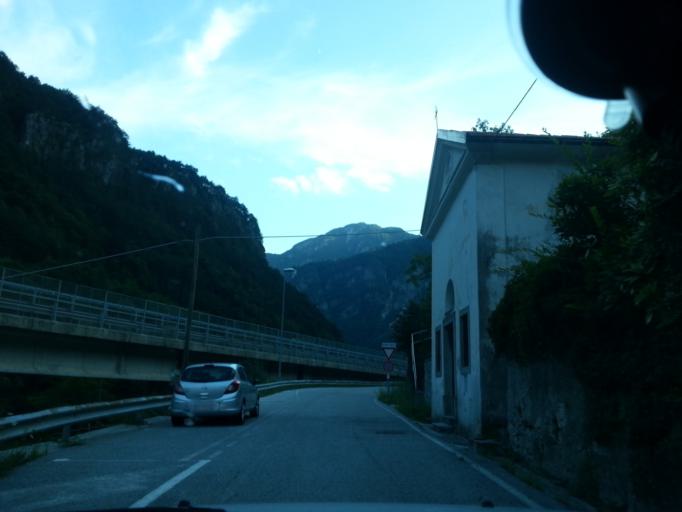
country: IT
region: Friuli Venezia Giulia
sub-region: Provincia di Udine
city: Dogna
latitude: 46.4441
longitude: 13.3134
